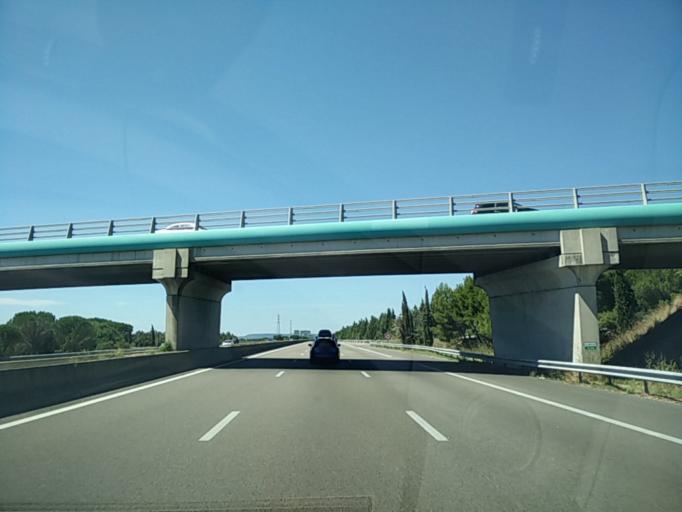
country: FR
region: Provence-Alpes-Cote d'Azur
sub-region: Departement du Vaucluse
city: Courthezon
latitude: 44.1099
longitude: 4.8440
